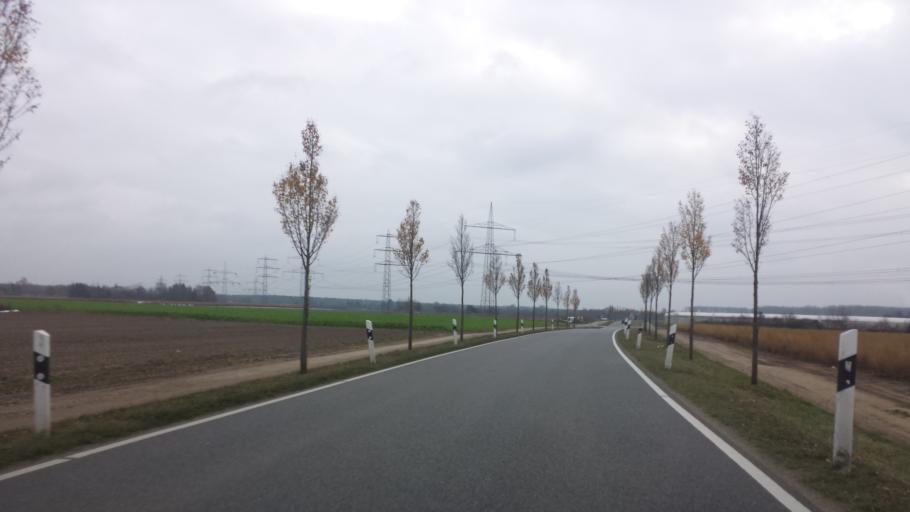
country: DE
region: Hesse
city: Lampertheim
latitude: 49.5938
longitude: 8.4958
